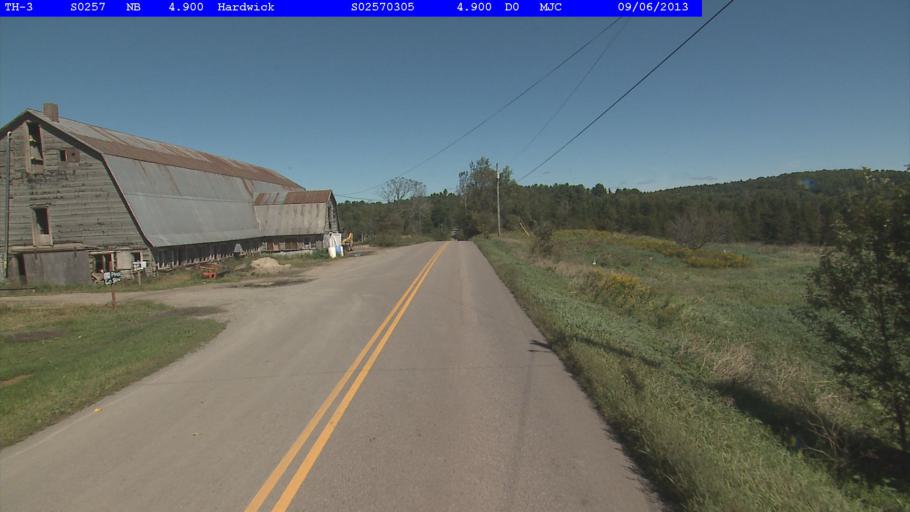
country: US
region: Vermont
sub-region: Caledonia County
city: Hardwick
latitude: 44.5572
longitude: -72.3150
